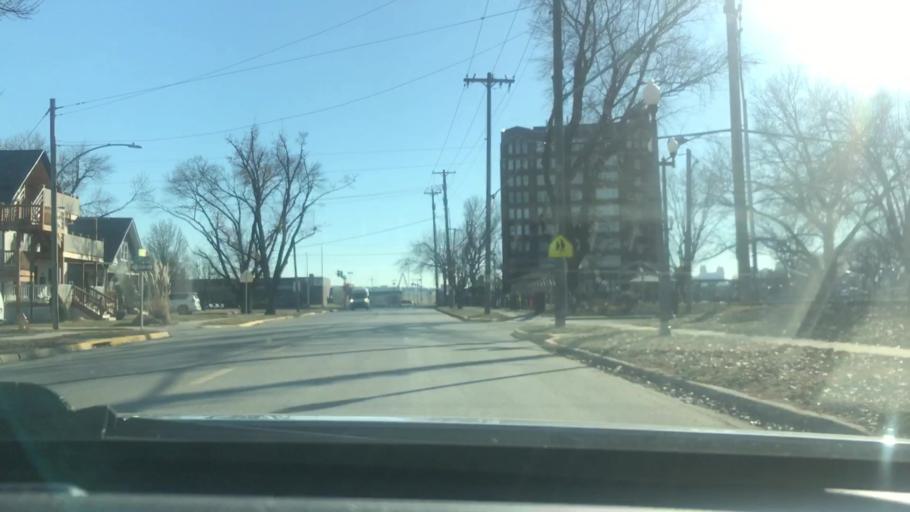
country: US
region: Missouri
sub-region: Clay County
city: North Kansas City
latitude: 39.1442
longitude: -94.5718
